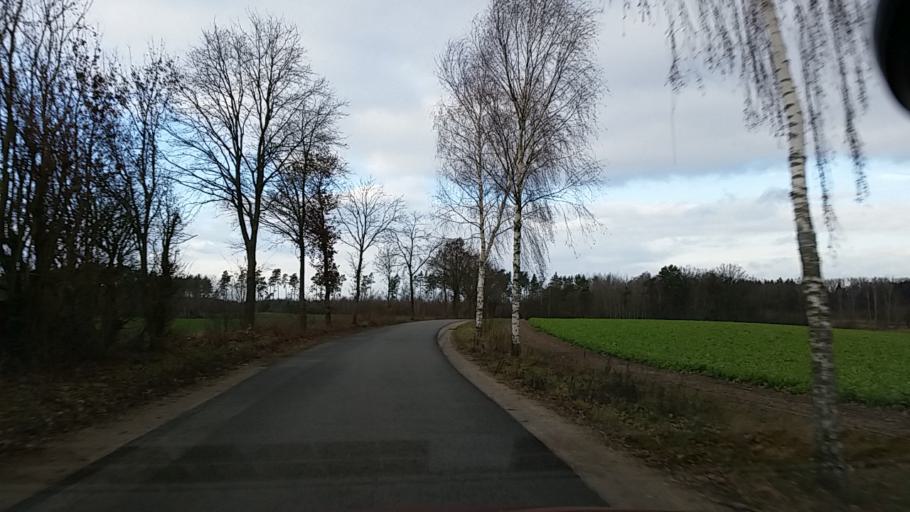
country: DE
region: Lower Saxony
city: Wieren
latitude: 52.8673
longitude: 10.6626
